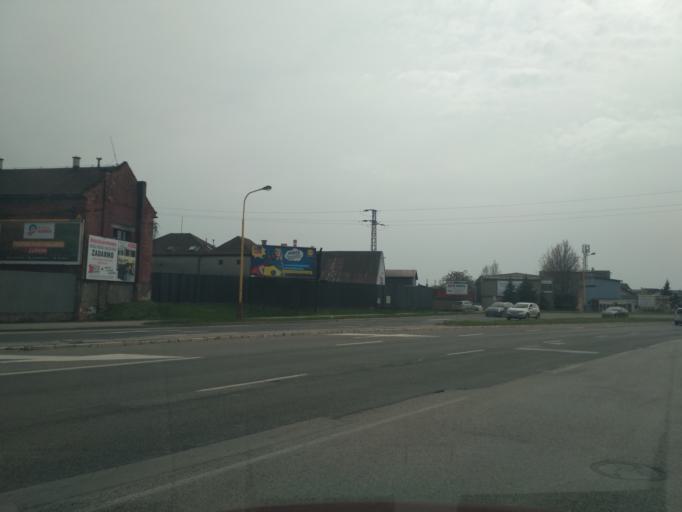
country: SK
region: Kosicky
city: Kosice
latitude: 48.7061
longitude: 21.2656
